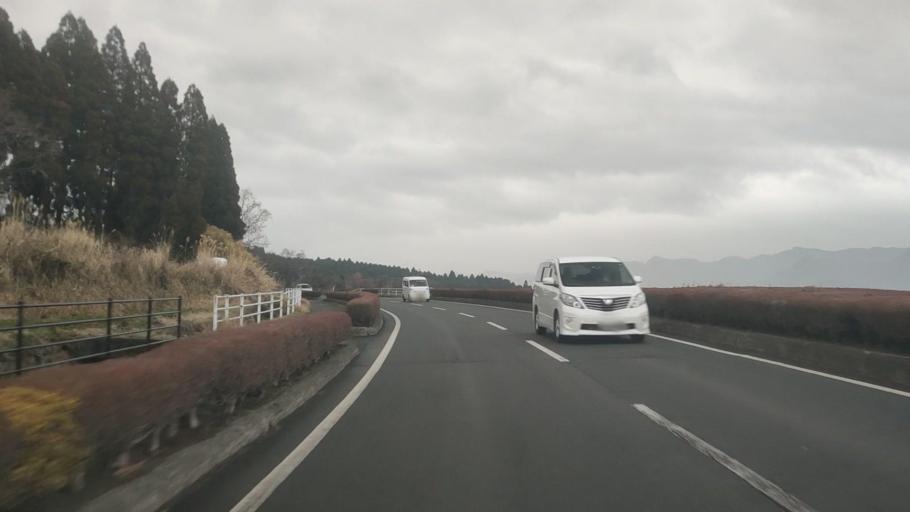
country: JP
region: Kumamoto
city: Aso
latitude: 32.8321
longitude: 131.0747
